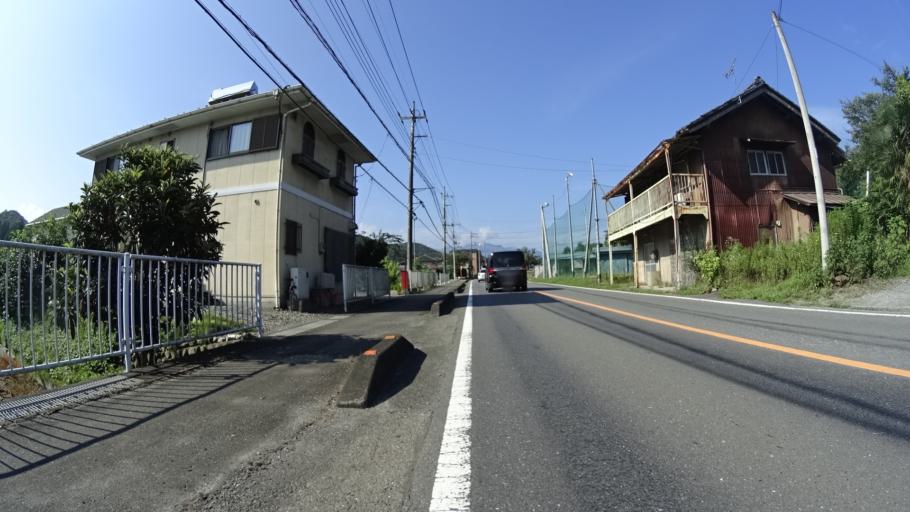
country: JP
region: Saitama
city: Chichibu
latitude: 36.0219
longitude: 139.0668
